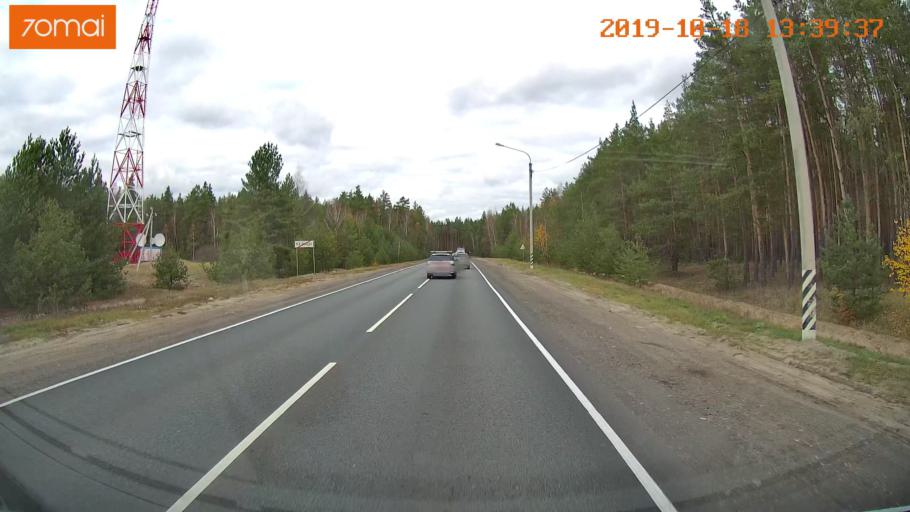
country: RU
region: Rjazan
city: Solotcha
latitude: 54.9009
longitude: 40.0026
